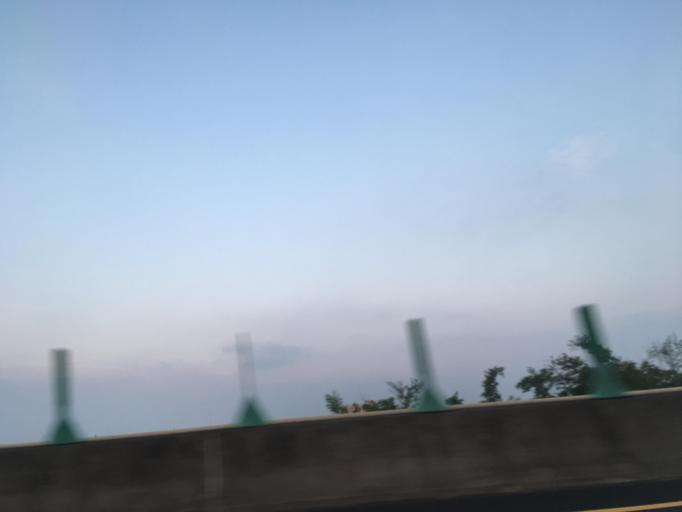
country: TW
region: Taiwan
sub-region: Yilan
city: Yilan
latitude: 24.7252
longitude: 121.7850
